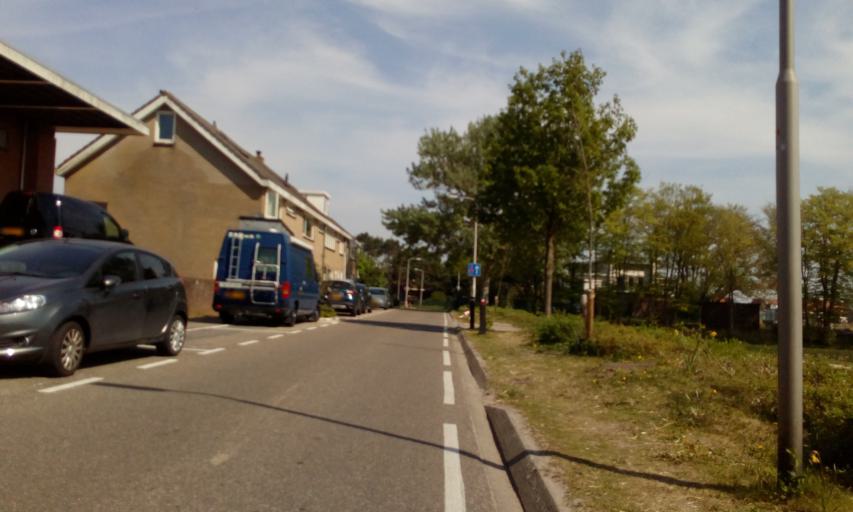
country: NL
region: South Holland
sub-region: Gemeente Hillegom
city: Hillegom
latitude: 52.2935
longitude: 4.5624
